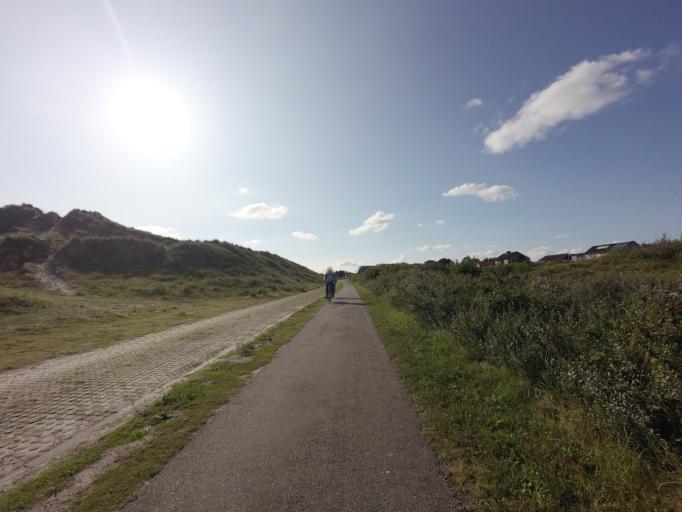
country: NL
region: Friesland
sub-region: Gemeente Terschelling
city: West-Terschelling
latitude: 53.3979
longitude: 5.2597
